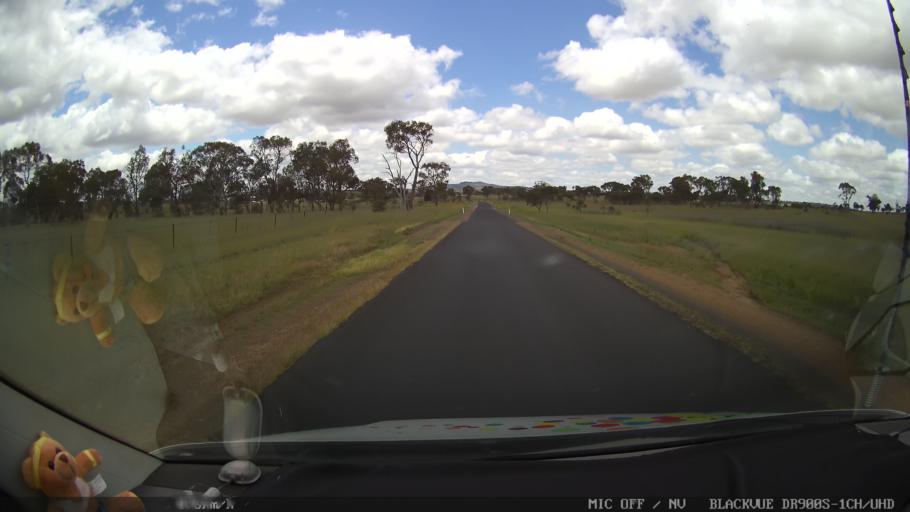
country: AU
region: New South Wales
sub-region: Glen Innes Severn
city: Glen Innes
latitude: -29.4389
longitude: 151.8336
